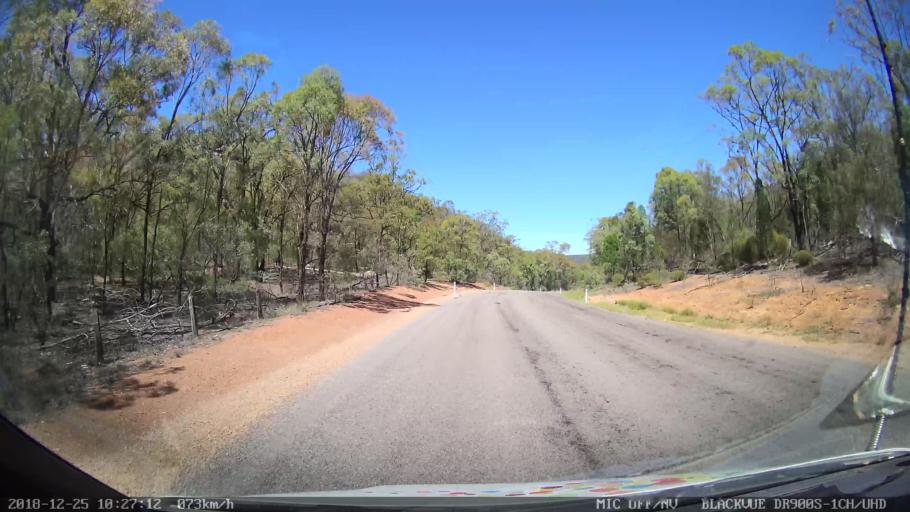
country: AU
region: New South Wales
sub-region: Muswellbrook
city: Denman
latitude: -32.3898
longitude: 150.4756
